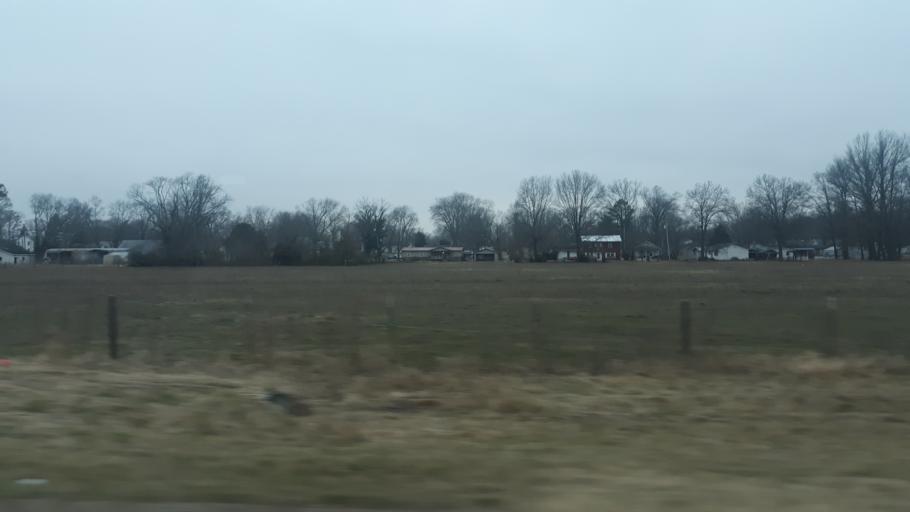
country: US
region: Illinois
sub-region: Saline County
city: Eldorado
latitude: 37.8143
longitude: -88.4270
